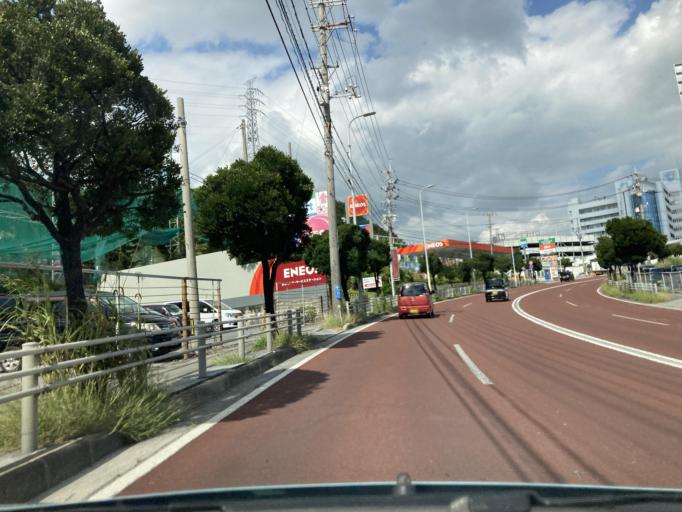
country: JP
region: Okinawa
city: Ginowan
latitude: 26.2358
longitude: 127.7696
